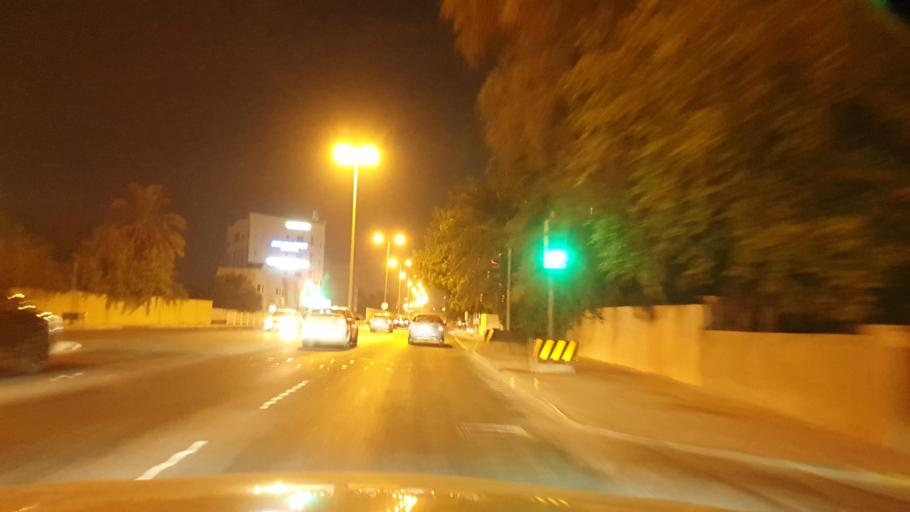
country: BH
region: Manama
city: Jidd Hafs
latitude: 26.2090
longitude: 50.5341
